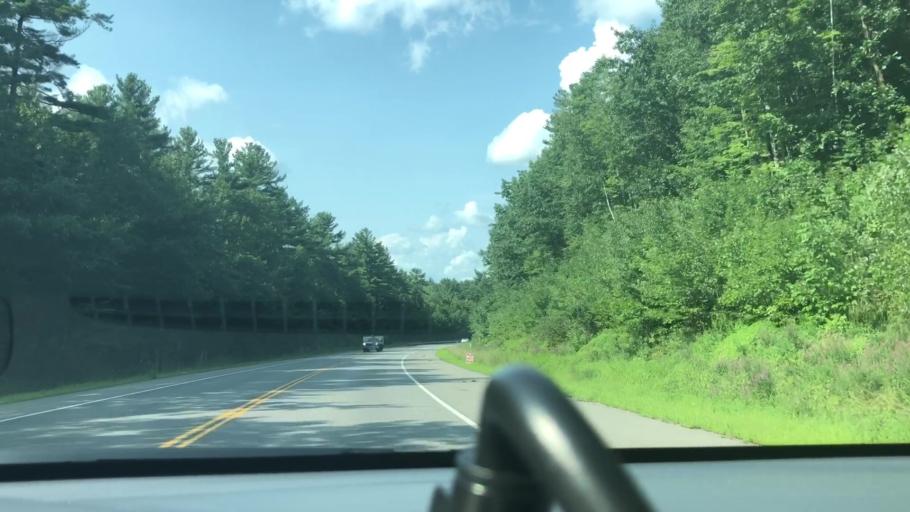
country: US
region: New Hampshire
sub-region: Hillsborough County
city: Pinardville
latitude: 42.9939
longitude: -71.5252
